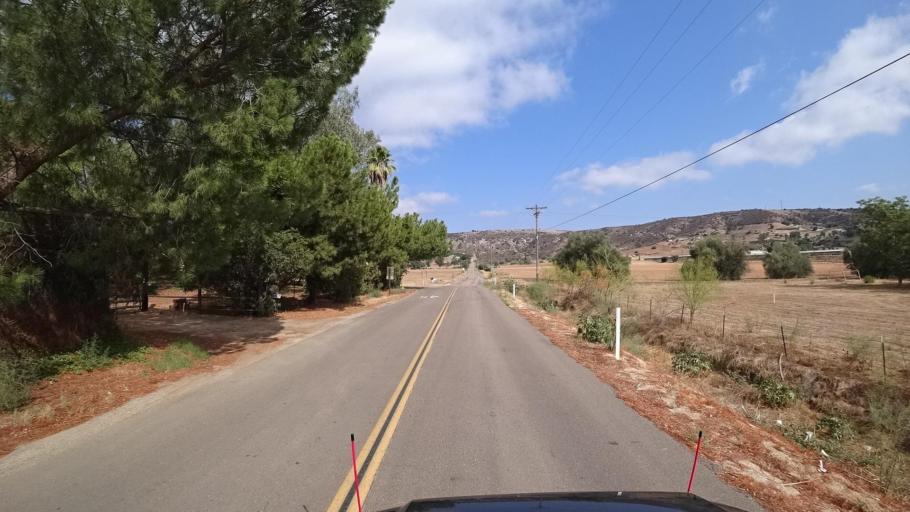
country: US
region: California
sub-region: San Diego County
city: Ramona
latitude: 33.0257
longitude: -116.8455
